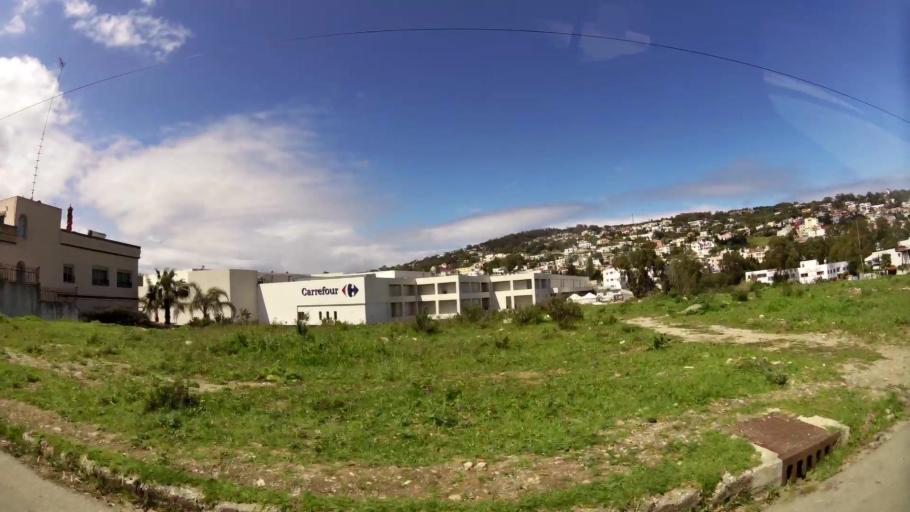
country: MA
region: Tanger-Tetouan
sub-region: Tanger-Assilah
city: Tangier
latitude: 35.7811
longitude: -5.8383
